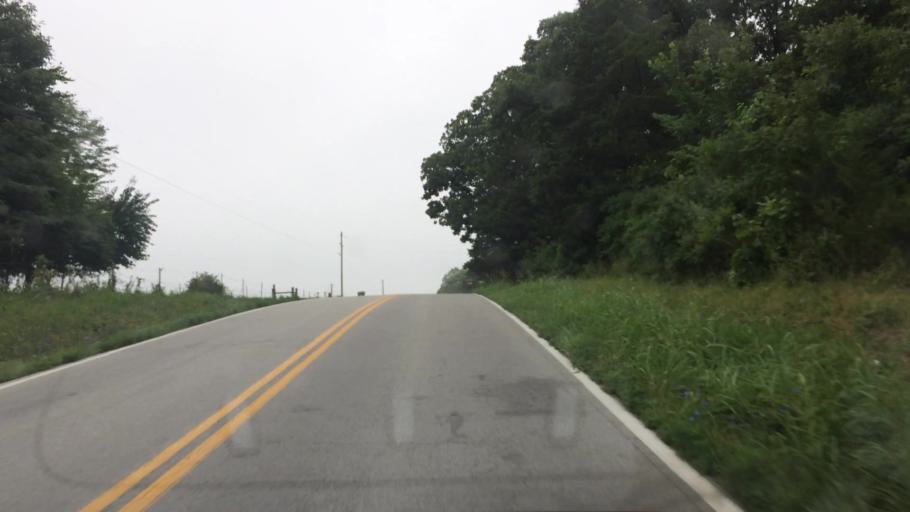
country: US
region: Missouri
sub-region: Greene County
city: Strafford
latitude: 37.2721
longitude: -93.1949
